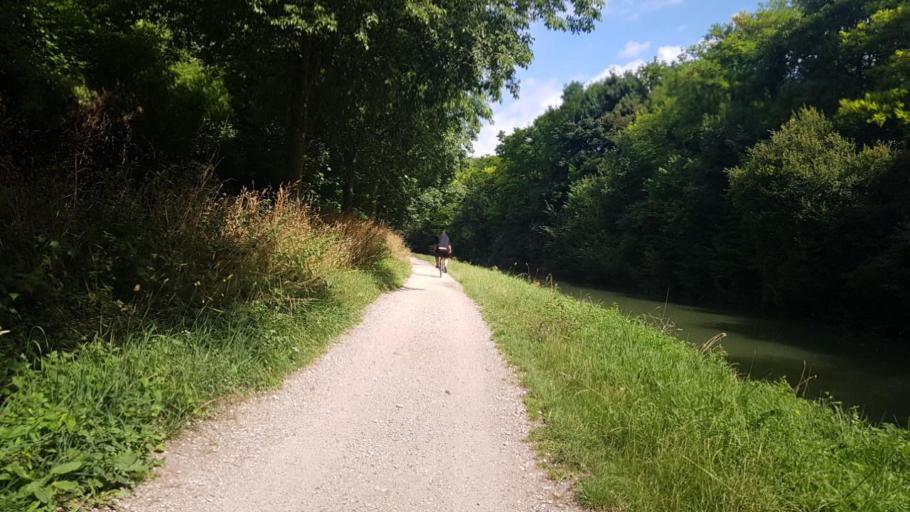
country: FR
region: Ile-de-France
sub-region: Departement de Seine-et-Marne
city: Claye-Souilly
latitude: 48.9577
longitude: 2.6767
